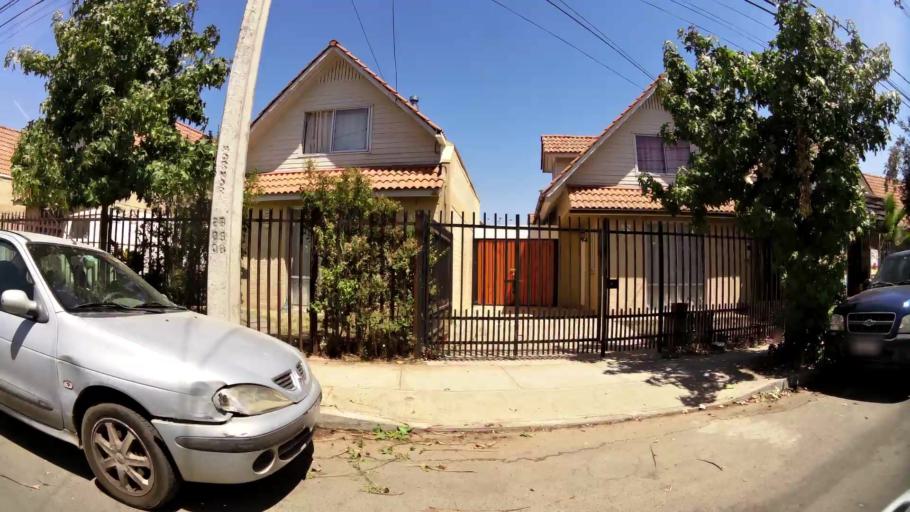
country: CL
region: Maule
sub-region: Provincia de Talca
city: Talca
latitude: -35.4306
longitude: -71.6242
